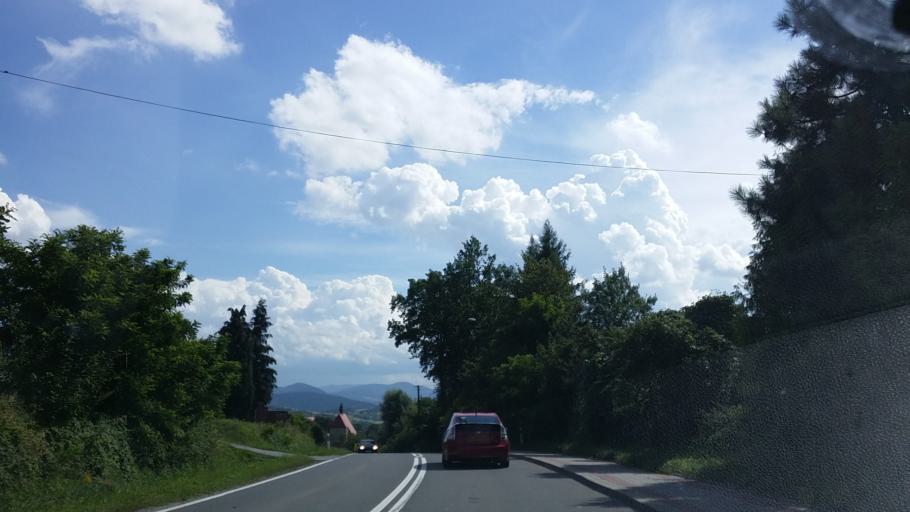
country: PL
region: Lesser Poland Voivodeship
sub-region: Powiat myslenicki
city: Dobczyce
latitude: 49.9054
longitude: 20.0973
